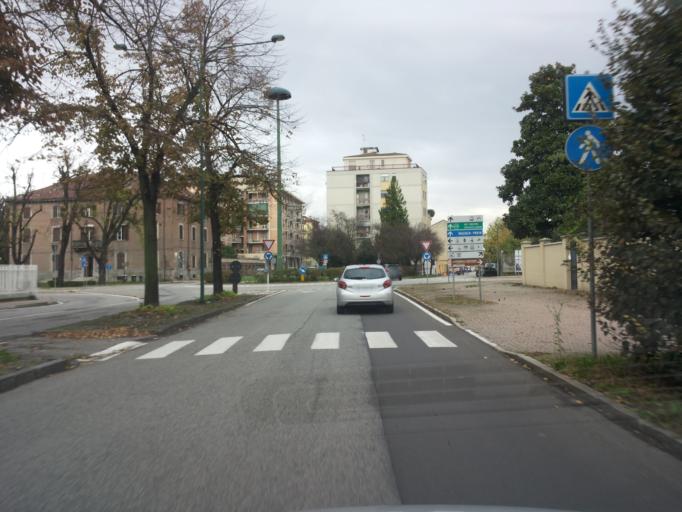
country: IT
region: Piedmont
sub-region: Provincia di Alessandria
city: Casale Monferrato
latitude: 45.1315
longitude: 8.4561
